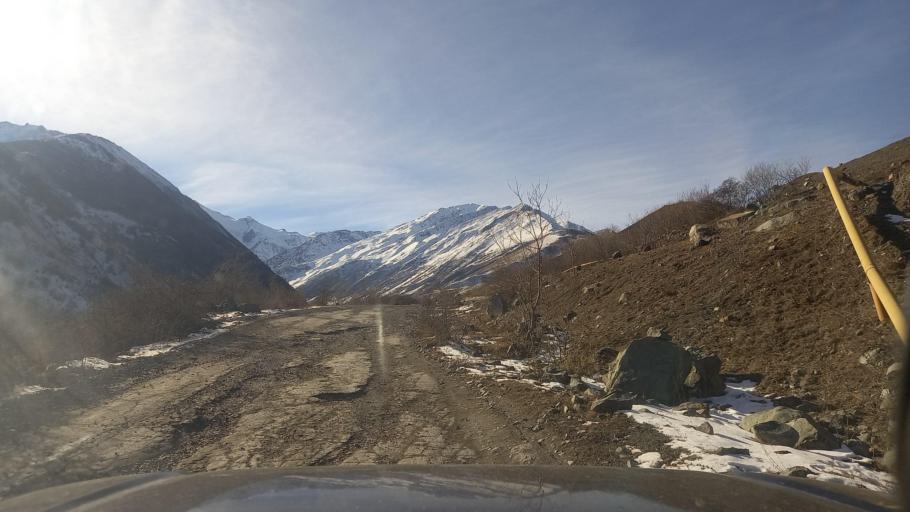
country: RU
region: Ingushetiya
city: Dzhayrakh
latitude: 42.8407
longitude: 44.5134
